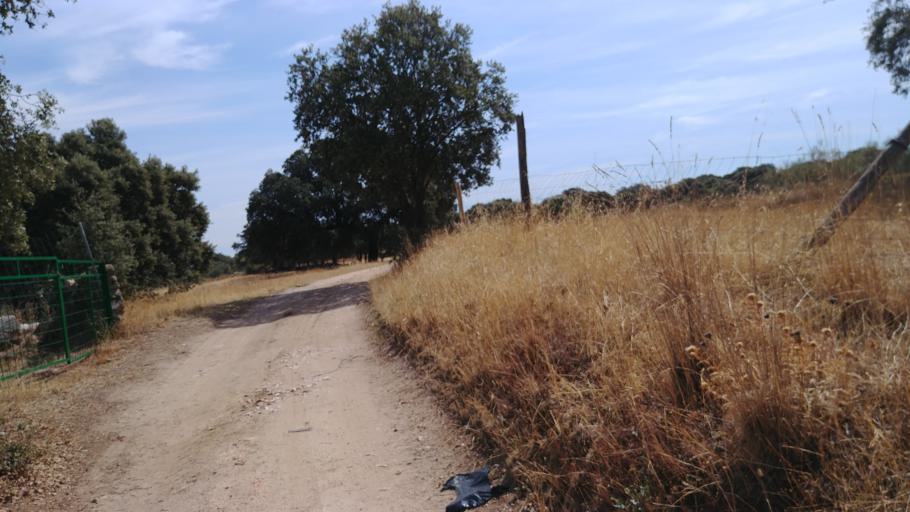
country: ES
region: Castille-La Mancha
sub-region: Province of Toledo
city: Navalcan
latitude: 40.0621
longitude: -5.0972
